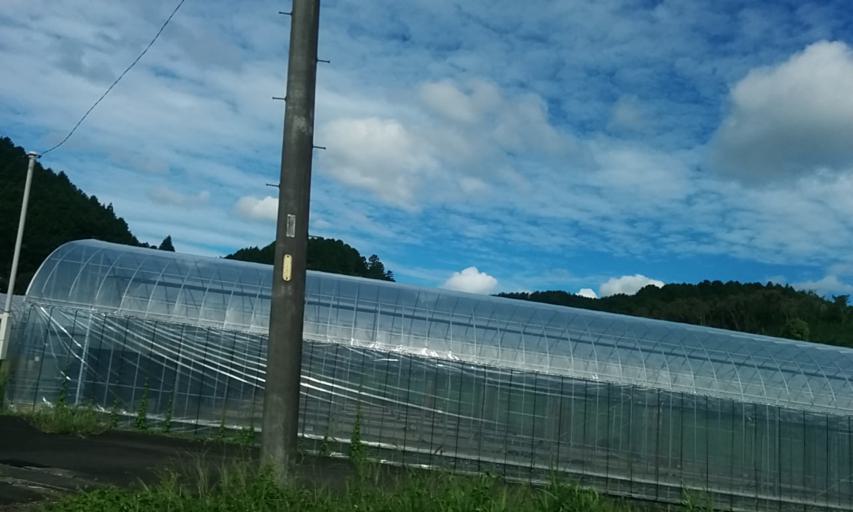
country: JP
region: Gifu
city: Minokamo
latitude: 35.5904
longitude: 137.0877
